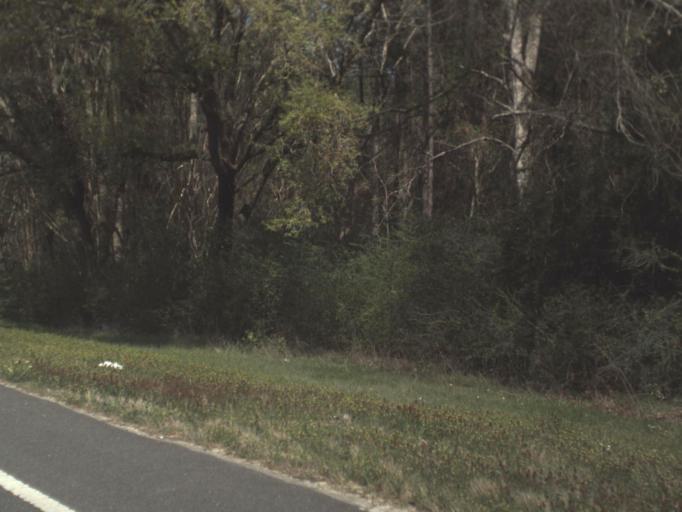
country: US
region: Florida
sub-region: Holmes County
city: Bonifay
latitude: 30.7936
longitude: -85.7187
